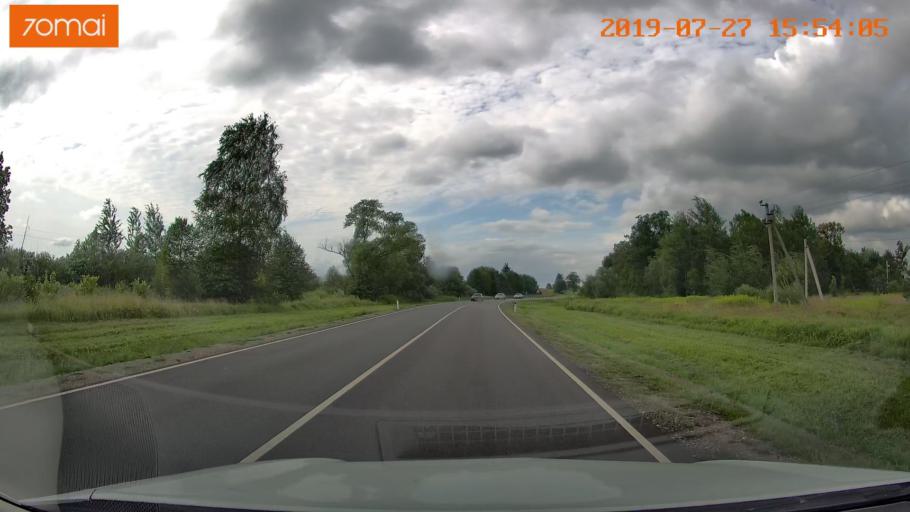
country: RU
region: Kaliningrad
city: Chernyakhovsk
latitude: 54.6058
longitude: 21.9440
